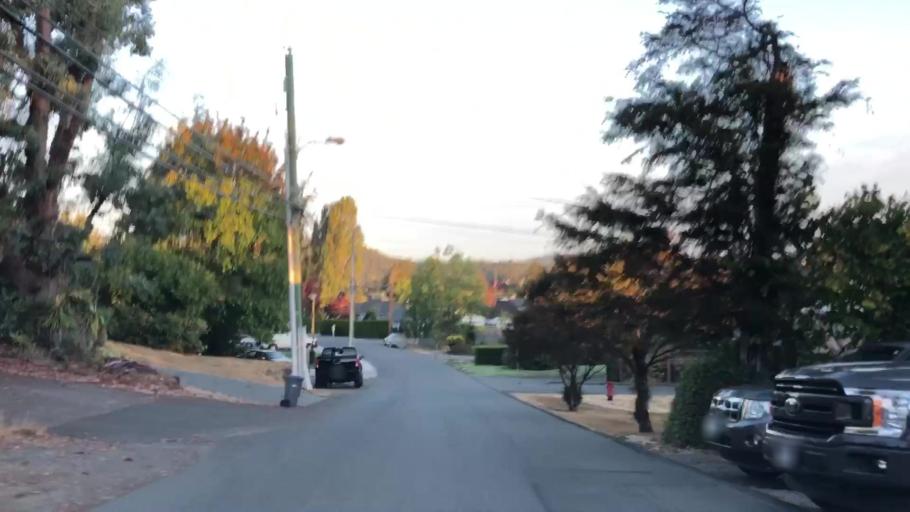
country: CA
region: British Columbia
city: Colwood
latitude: 48.4574
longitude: -123.4401
